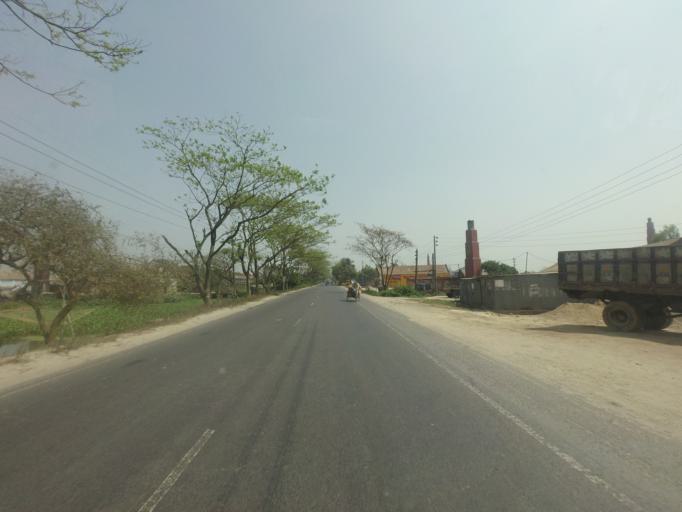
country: BD
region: Dhaka
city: Bhairab Bazar
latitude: 24.0392
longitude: 91.0315
